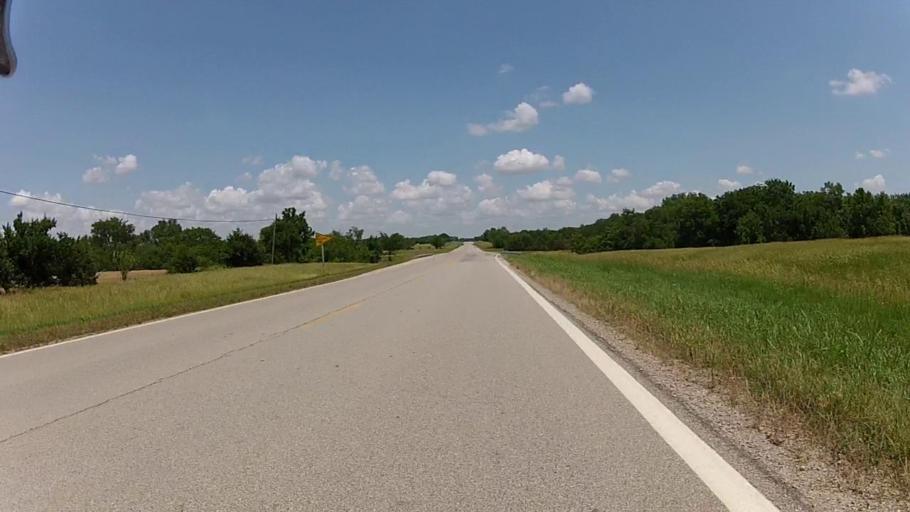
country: US
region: Kansas
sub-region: Labette County
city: Altamont
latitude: 37.1924
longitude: -95.4154
